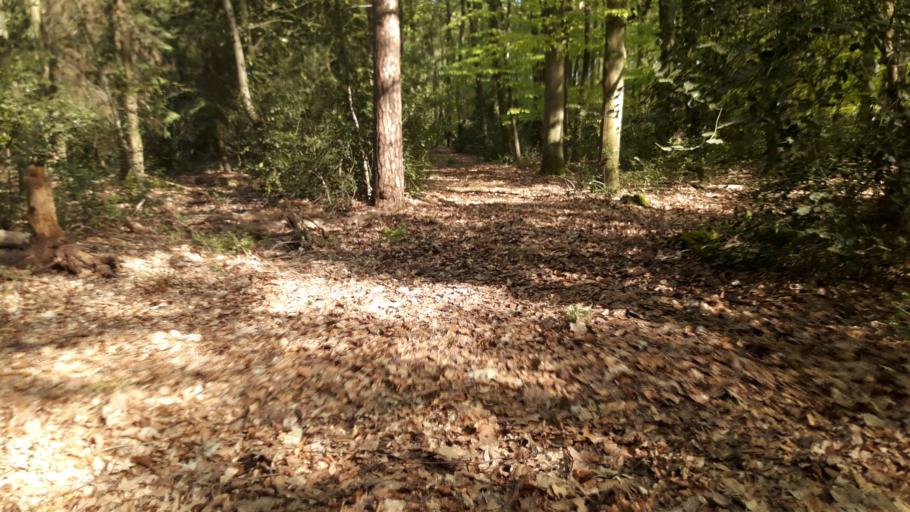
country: DE
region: North Rhine-Westphalia
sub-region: Regierungsbezirk Detmold
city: Salzkotten
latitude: 51.7057
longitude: 8.6664
